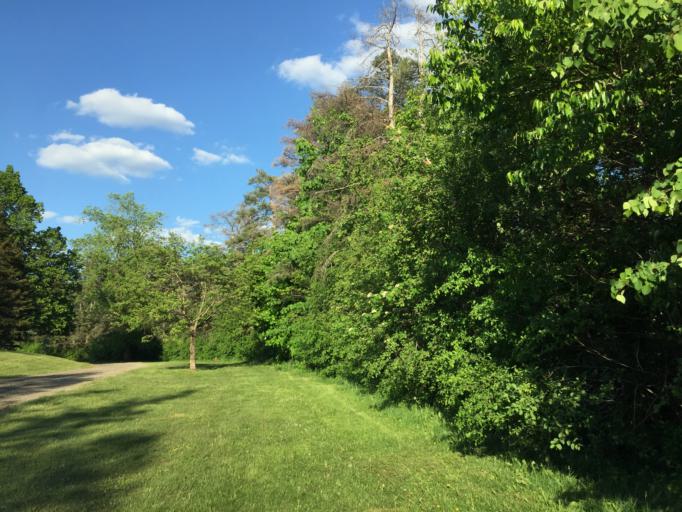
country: CA
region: Ontario
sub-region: Wellington County
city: Guelph
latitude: 43.5126
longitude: -80.3504
